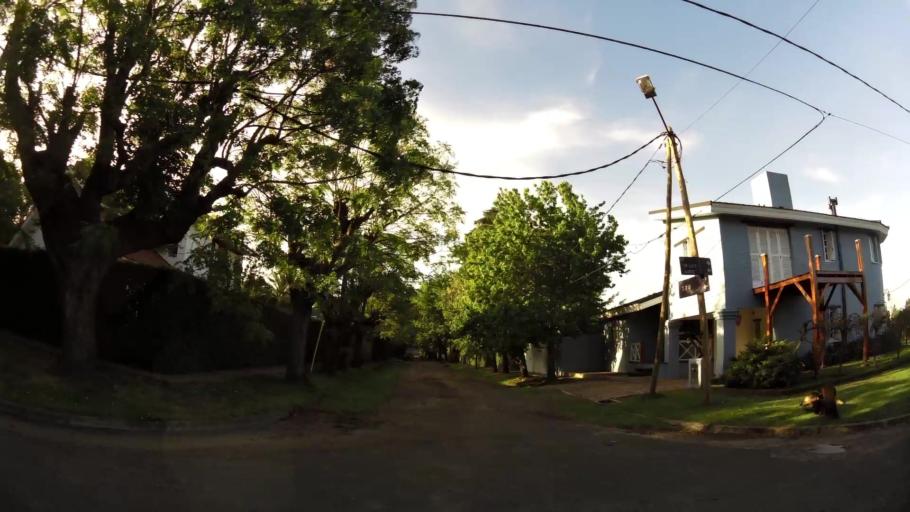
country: AR
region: Buenos Aires
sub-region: Partido de Quilmes
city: Quilmes
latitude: -34.7842
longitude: -58.2010
